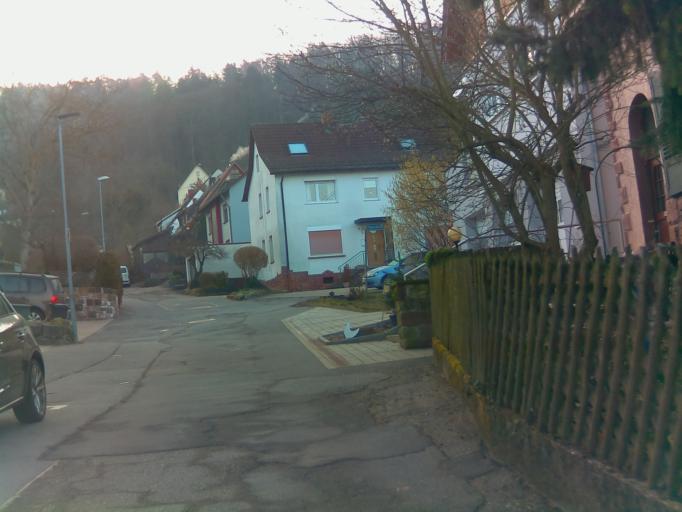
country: DE
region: Baden-Wuerttemberg
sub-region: Karlsruhe Region
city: Mosbach
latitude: 49.3500
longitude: 9.1502
